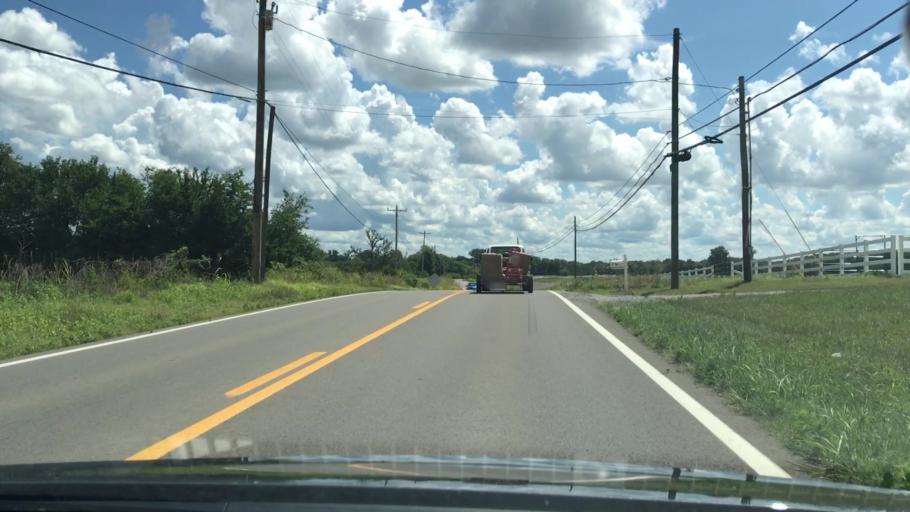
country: US
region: Tennessee
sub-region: Rutherford County
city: Murfreesboro
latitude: 35.8428
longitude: -86.5249
